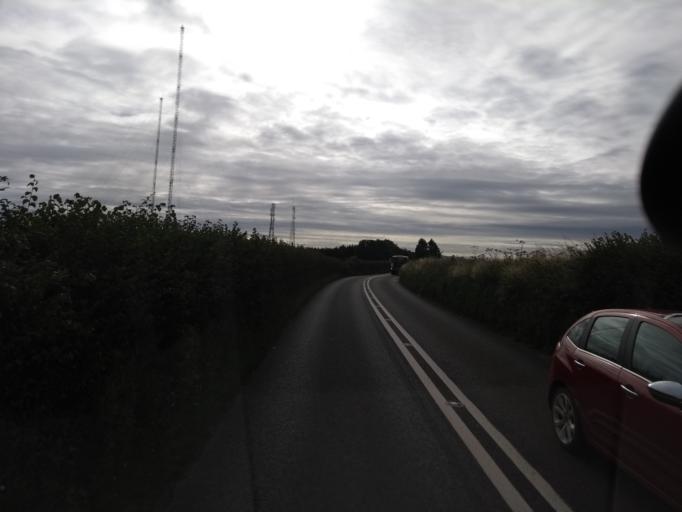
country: GB
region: England
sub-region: Somerset
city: Watchet
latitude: 51.1605
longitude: -3.3542
